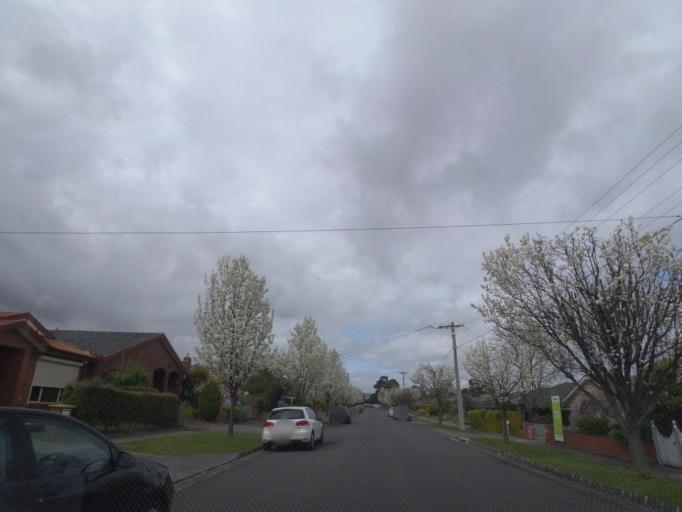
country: AU
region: Victoria
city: Mitcham
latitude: -37.8148
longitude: 145.1894
